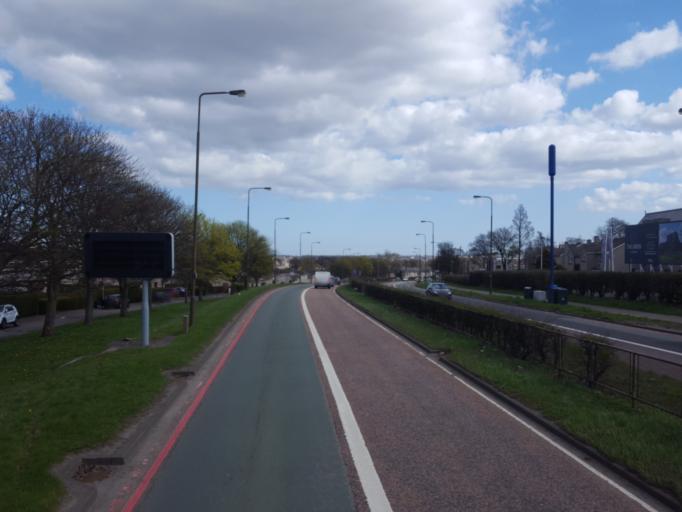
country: GB
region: Scotland
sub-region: Edinburgh
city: Colinton
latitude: 55.9272
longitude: -3.2675
